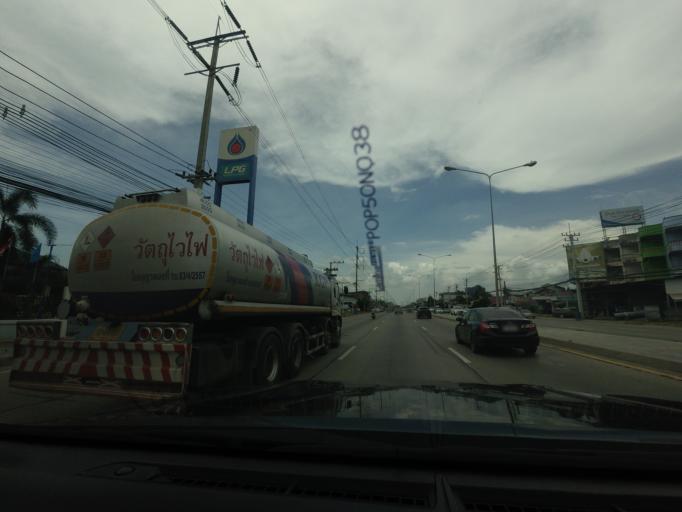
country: TH
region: Nakhon Pathom
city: Nakhon Pathom
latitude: 13.8419
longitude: 100.0269
